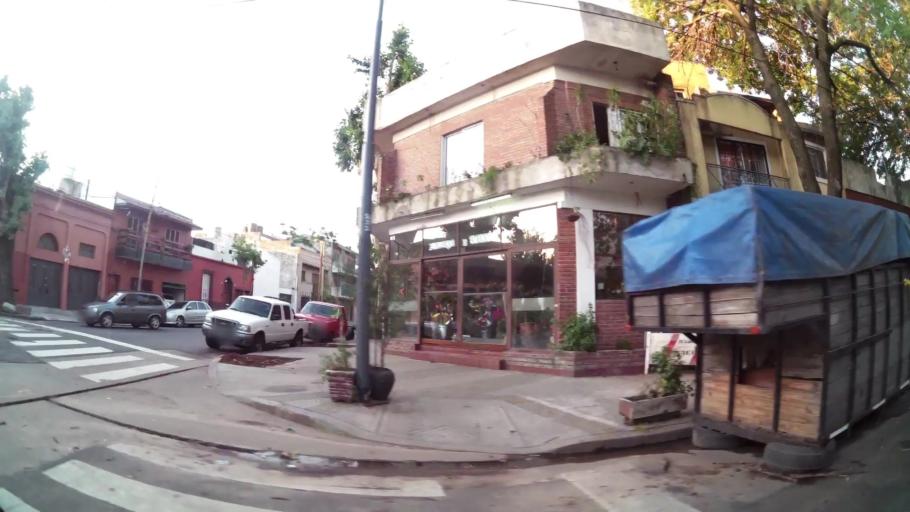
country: AR
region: Buenos Aires F.D.
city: Buenos Aires
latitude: -34.6329
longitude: -58.4114
